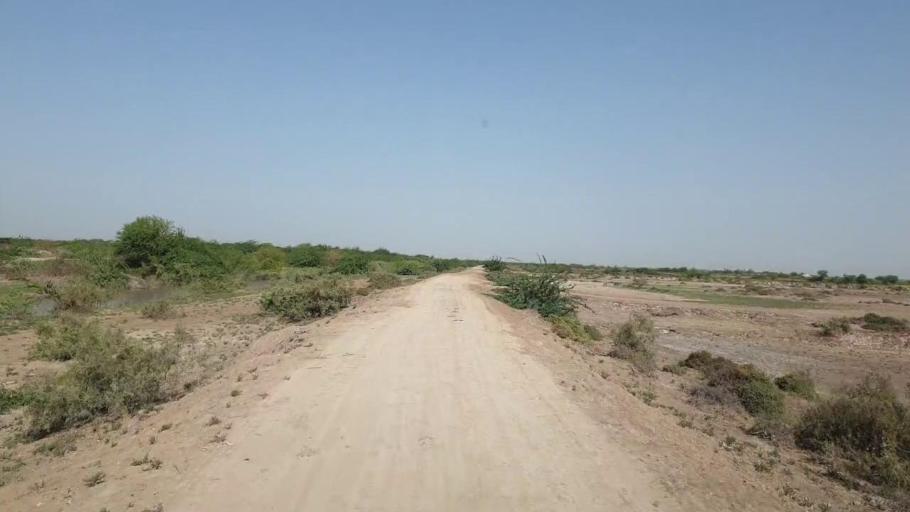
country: PK
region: Sindh
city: Tando Bago
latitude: 24.6510
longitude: 69.0709
